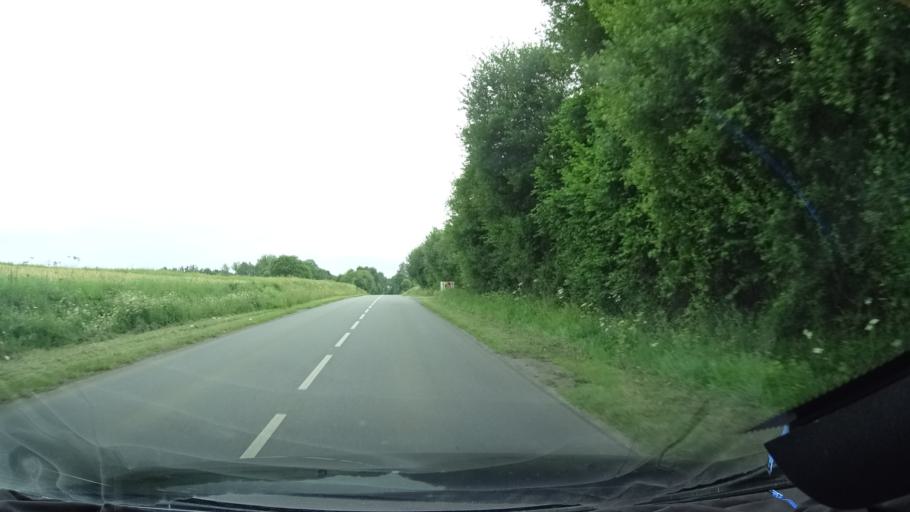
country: FR
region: Brittany
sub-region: Departement d'Ille-et-Vilaine
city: Le Minihic-sur-Rance
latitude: 48.5708
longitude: -2.0158
